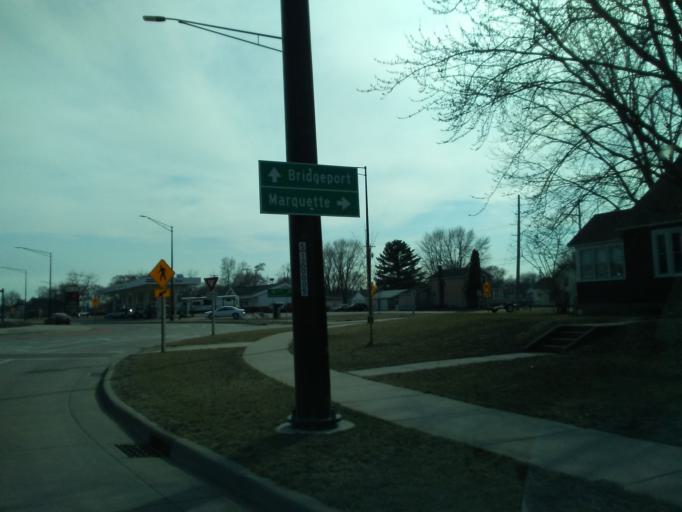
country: US
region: Wisconsin
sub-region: Crawford County
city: Prairie du Chien
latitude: 43.0509
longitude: -91.1411
